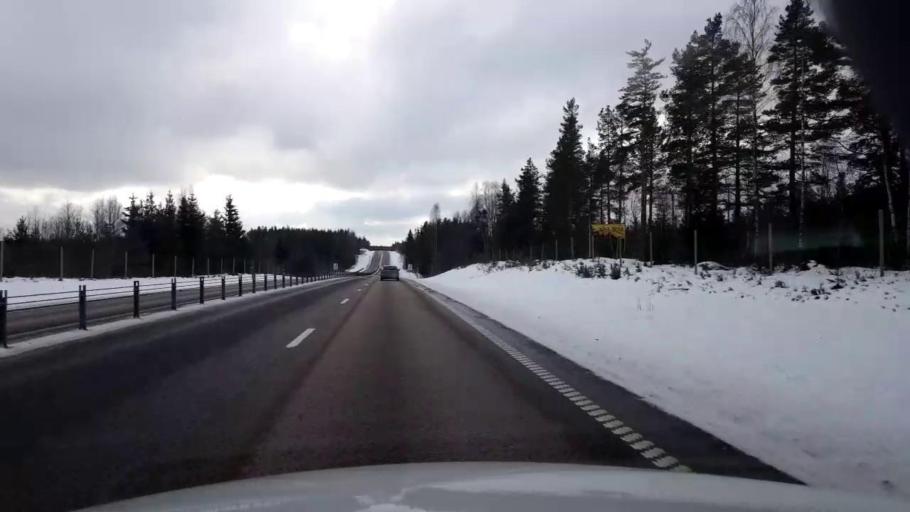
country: SE
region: Gaevleborg
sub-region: Hudiksvalls Kommun
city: Hudiksvall
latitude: 61.8241
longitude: 17.1916
